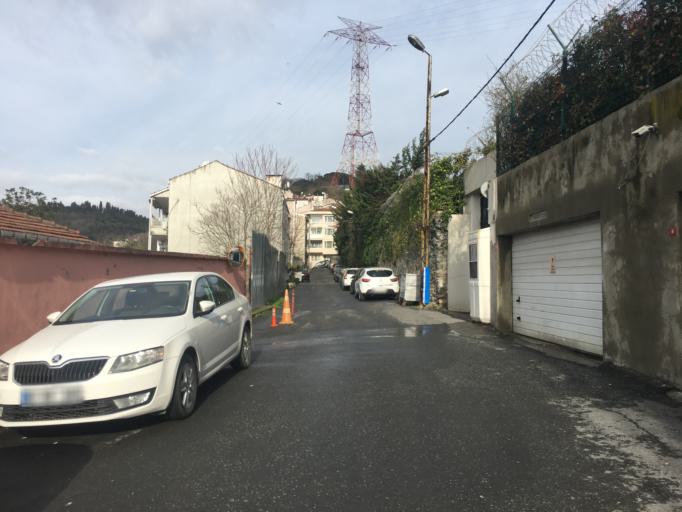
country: TR
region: Istanbul
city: UEskuedar
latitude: 41.0697
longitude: 29.0436
